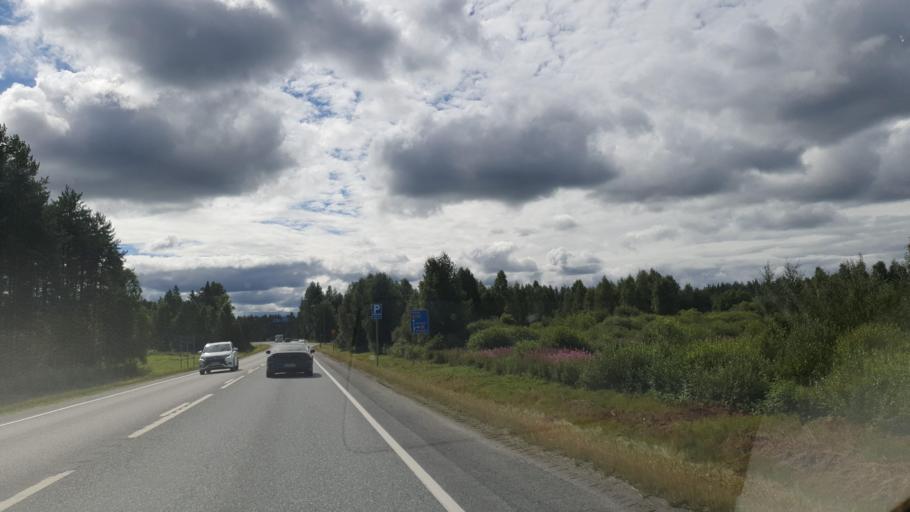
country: FI
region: Kainuu
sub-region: Kajaani
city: Kajaani
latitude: 64.1208
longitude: 27.4573
